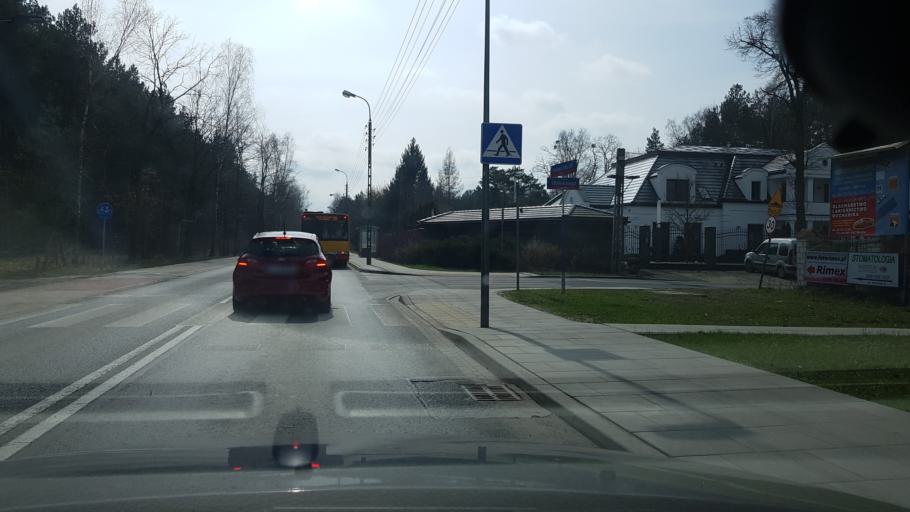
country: PL
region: Masovian Voivodeship
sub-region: Warszawa
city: Wesola
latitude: 52.2425
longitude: 21.2227
